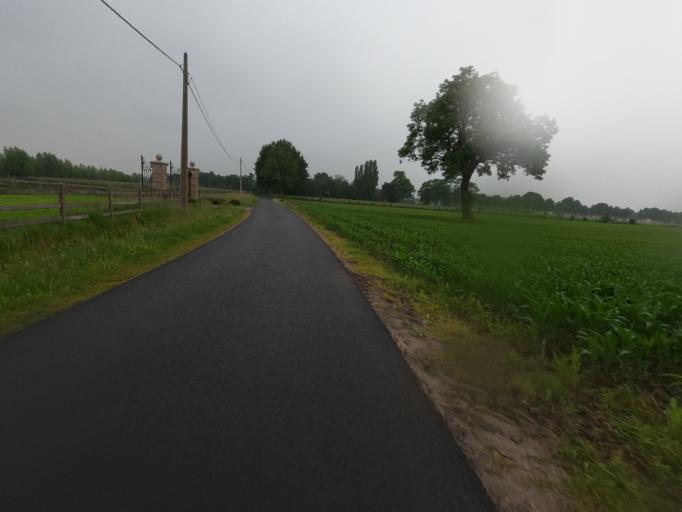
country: BE
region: Flanders
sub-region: Provincie Antwerpen
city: Essen
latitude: 51.4300
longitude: 4.5150
